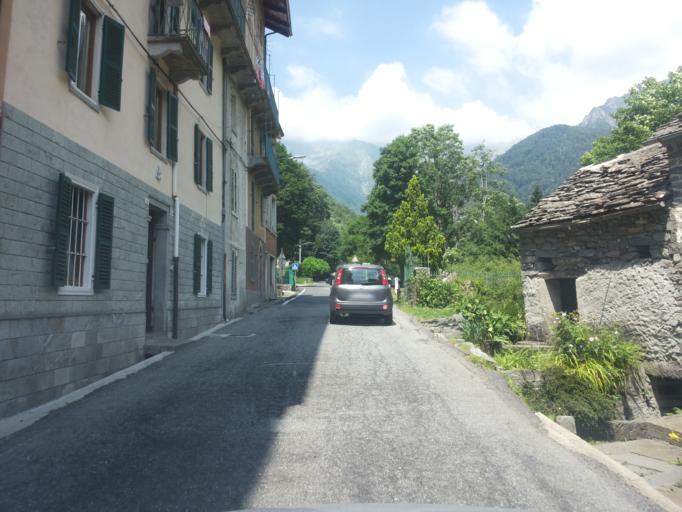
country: IT
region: Piedmont
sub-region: Provincia di Biella
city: Rosazza
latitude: 45.6791
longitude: 7.9749
